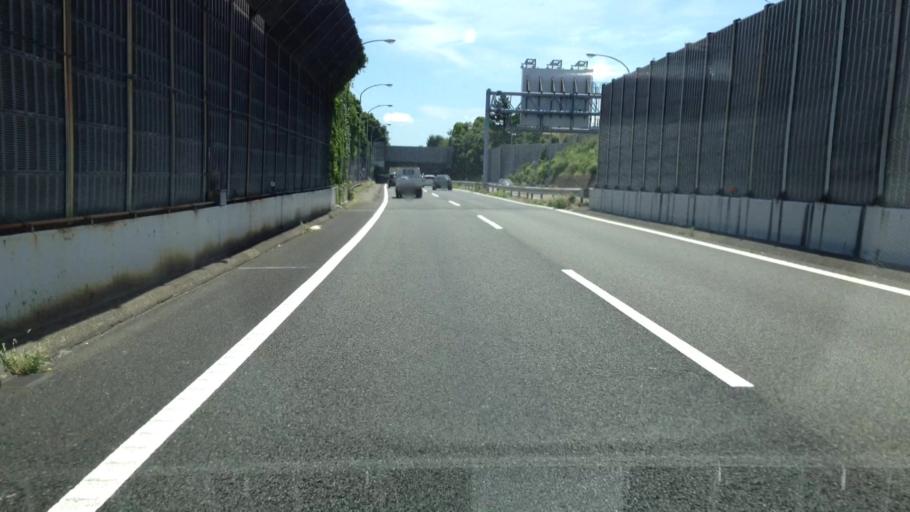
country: JP
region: Kanagawa
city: Yokohama
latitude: 35.4068
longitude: 139.5750
